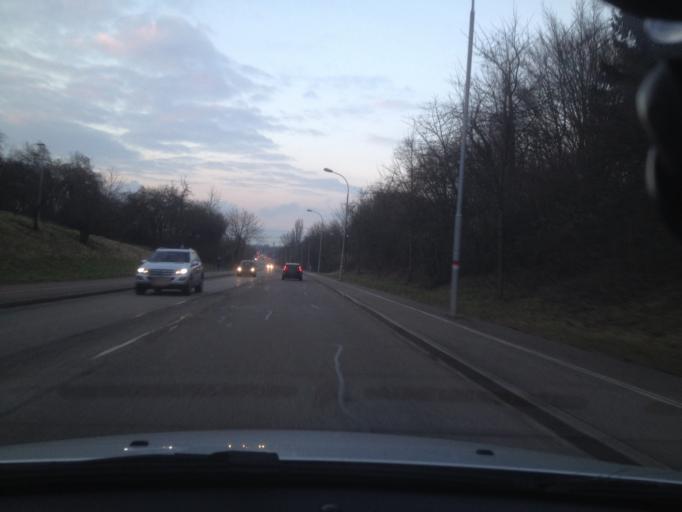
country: DE
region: Baden-Wuerttemberg
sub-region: Karlsruhe Region
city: Ettlingen
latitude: 48.9528
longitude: 8.4067
